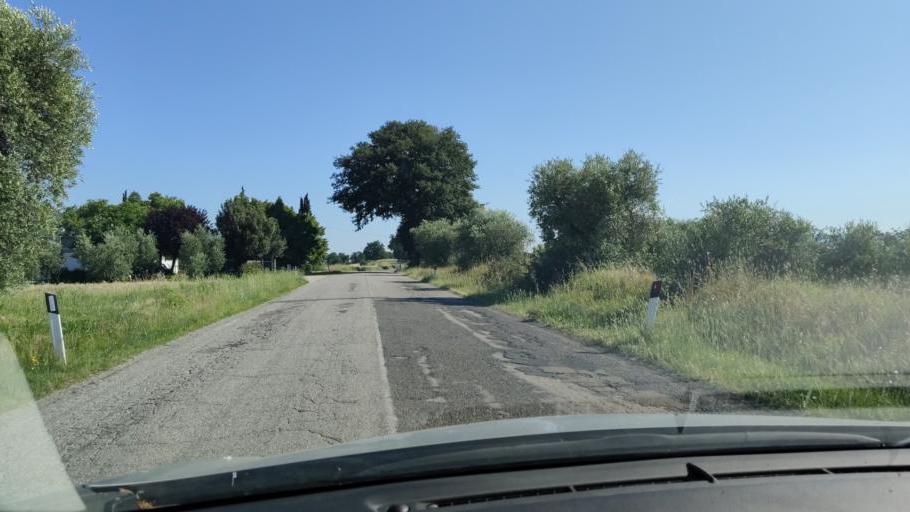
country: IT
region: Umbria
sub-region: Provincia di Terni
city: Avigliano Umbro
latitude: 42.6653
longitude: 12.4405
